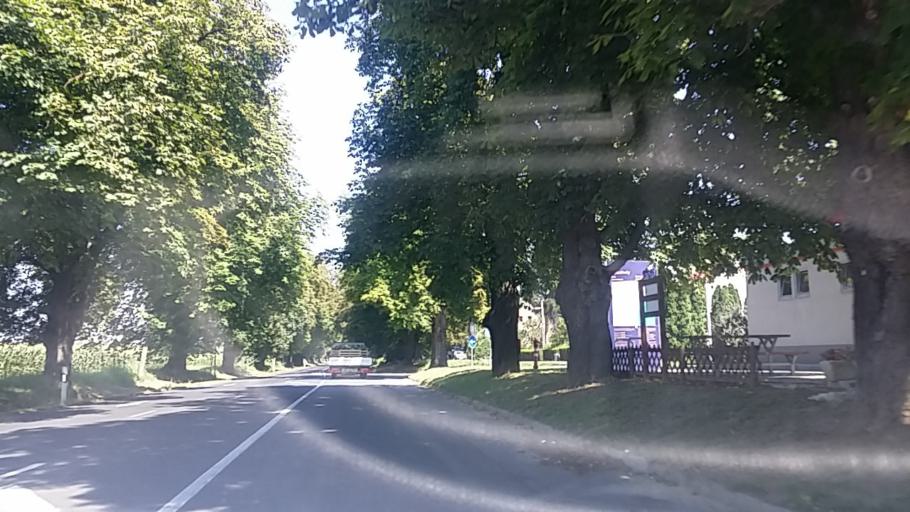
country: HU
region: Zala
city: Keszthely
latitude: 46.7417
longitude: 17.2405
